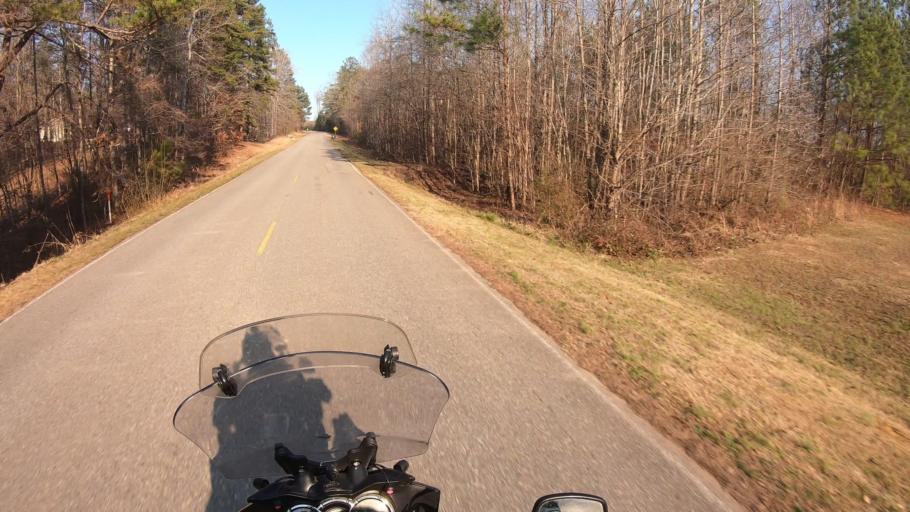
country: US
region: Alabama
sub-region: Cleburne County
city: Heflin
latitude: 33.7519
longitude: -85.4649
